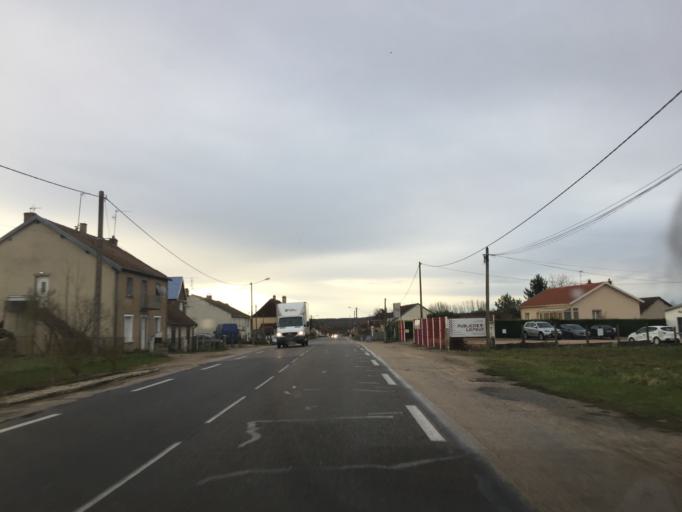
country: FR
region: Franche-Comte
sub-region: Departement du Jura
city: Choisey
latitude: 47.0495
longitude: 5.4944
